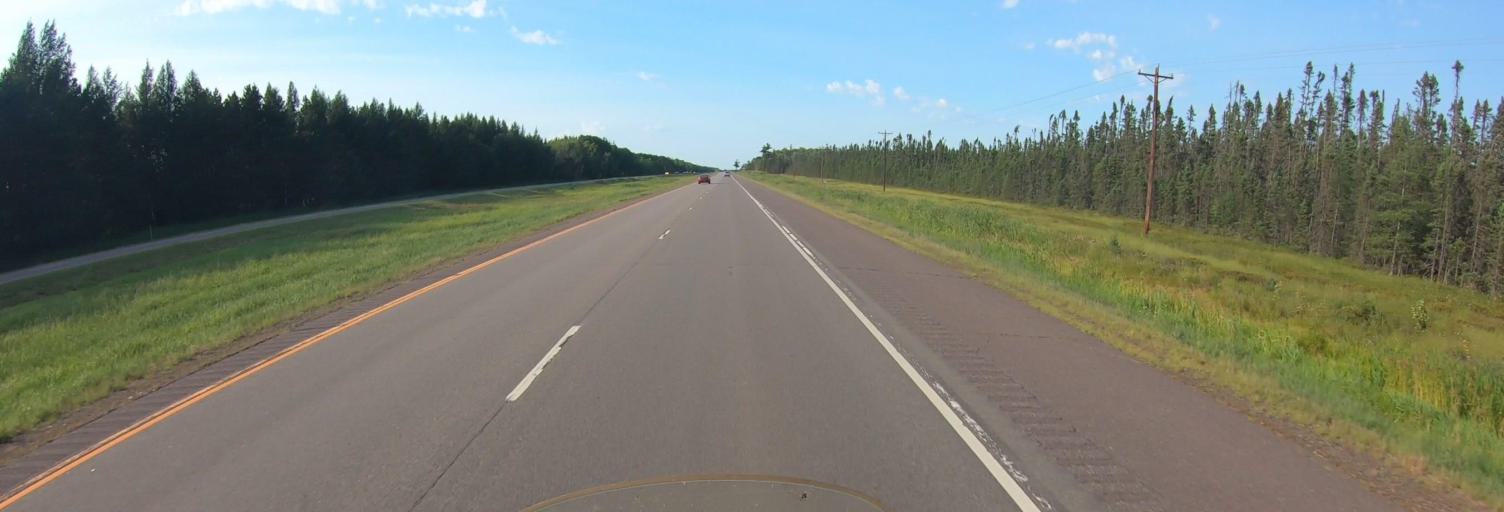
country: US
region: Minnesota
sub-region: Saint Louis County
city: Hermantown
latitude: 47.0944
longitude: -92.4715
